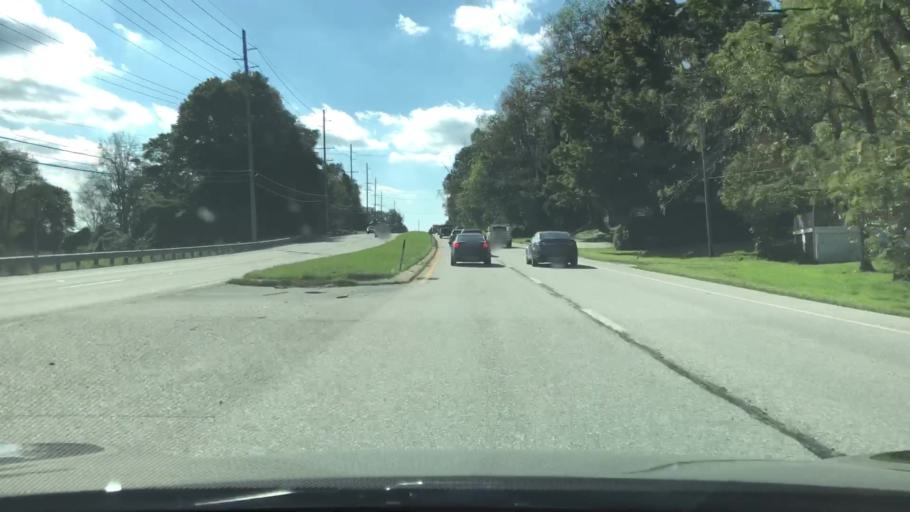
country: US
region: Pennsylvania
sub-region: Delaware County
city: Lima
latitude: 39.9726
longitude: -75.4627
